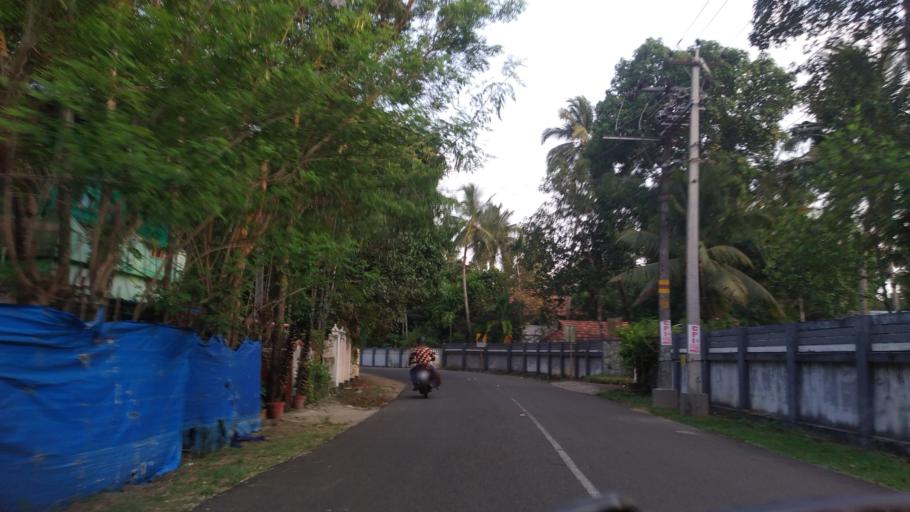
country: IN
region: Kerala
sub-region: Thrissur District
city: Thanniyam
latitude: 10.3355
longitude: 76.1190
